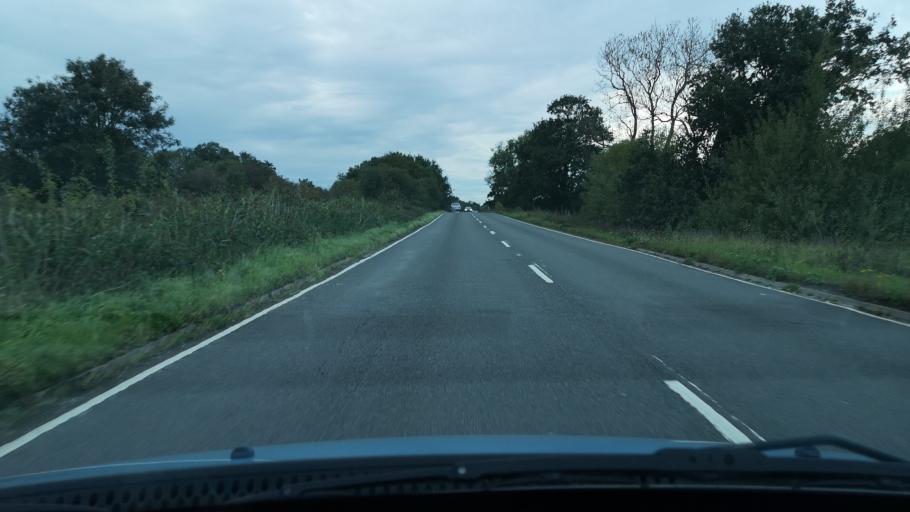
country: GB
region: England
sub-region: North Lincolnshire
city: Belton
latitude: 53.5827
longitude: -0.8059
